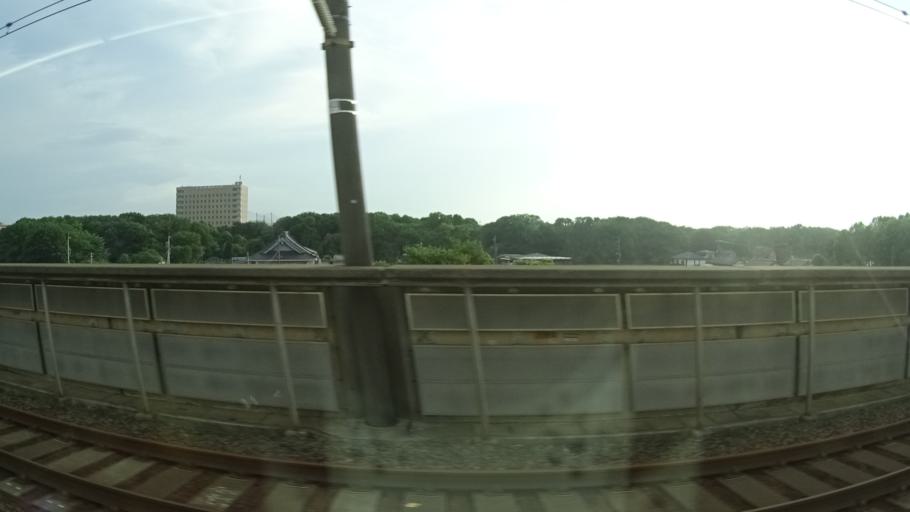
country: JP
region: Saitama
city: Ageoshimo
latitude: 35.9943
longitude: 139.6209
